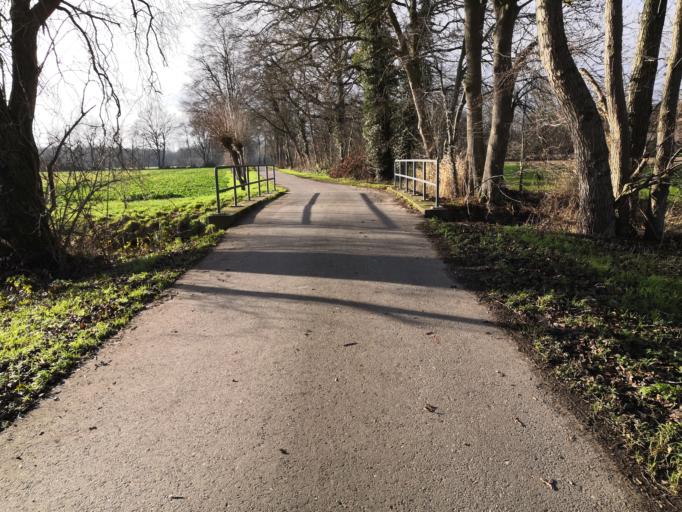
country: DE
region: North Rhine-Westphalia
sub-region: Regierungsbezirk Dusseldorf
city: Wachtendonk
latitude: 51.4431
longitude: 6.3652
